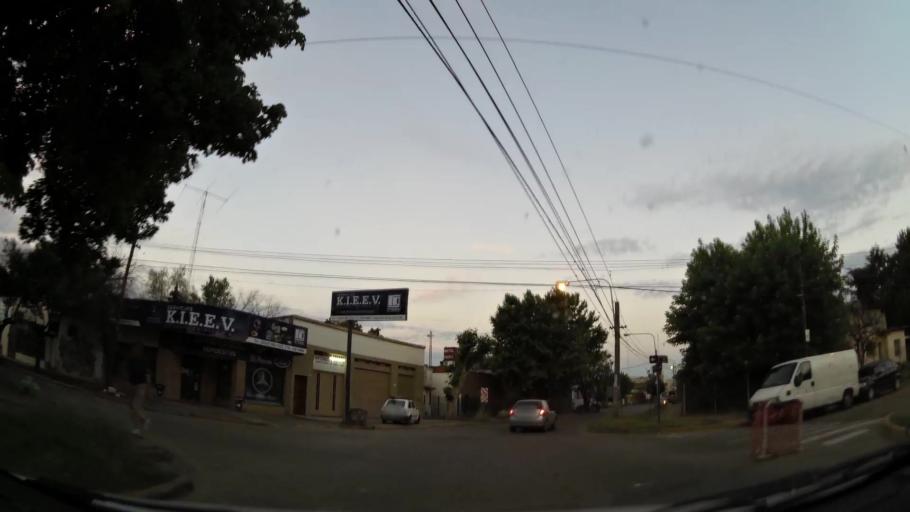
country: AR
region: Buenos Aires
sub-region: Partido de Merlo
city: Merlo
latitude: -34.6646
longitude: -58.7327
